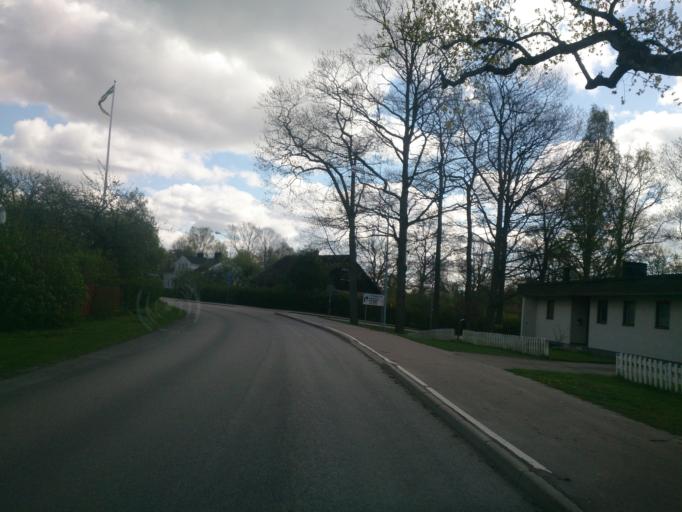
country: SE
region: OEstergoetland
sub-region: Atvidabergs Kommun
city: Atvidaberg
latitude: 58.1958
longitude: 15.9879
